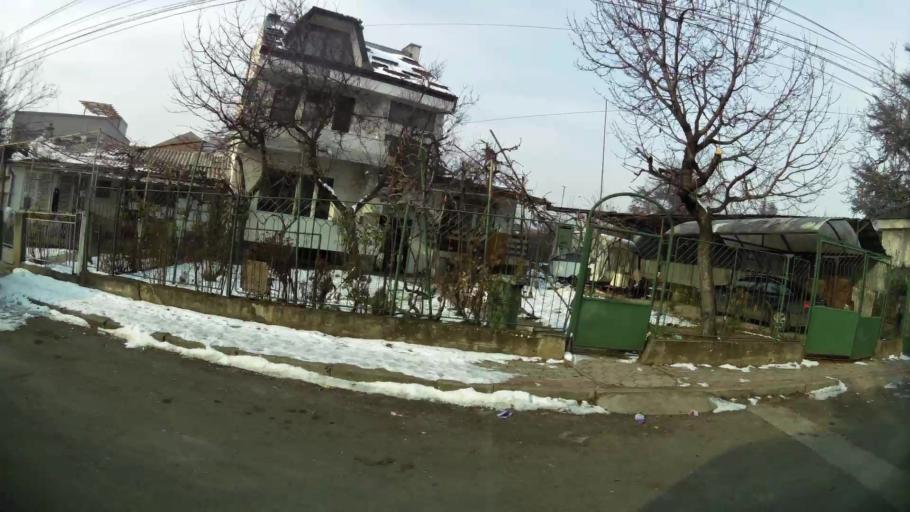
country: MK
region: Butel
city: Butel
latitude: 42.0207
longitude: 21.4532
